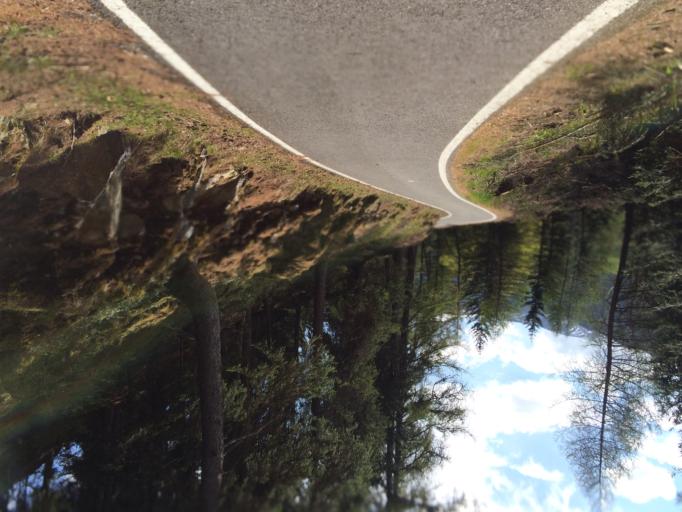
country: IT
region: Trentino-Alto Adige
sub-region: Bolzano
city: Malles Venosta
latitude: 46.7462
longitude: 10.5286
